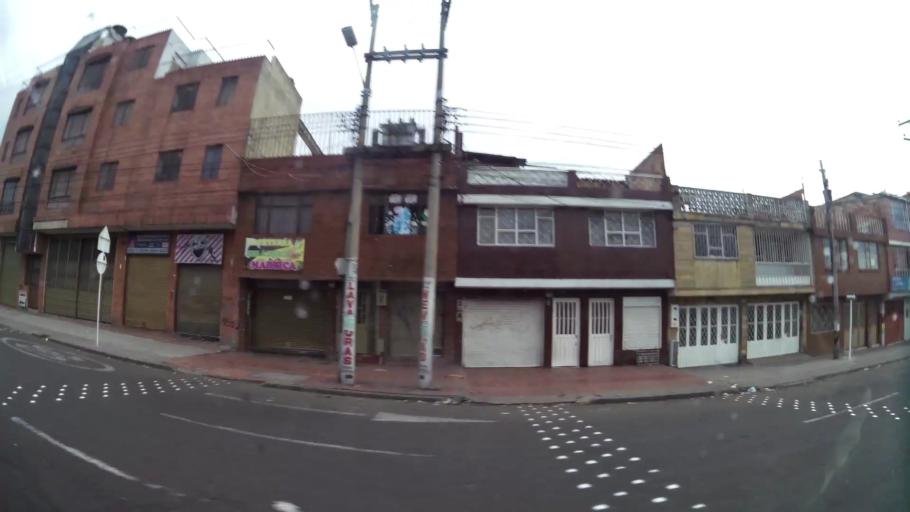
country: CO
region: Bogota D.C.
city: Bogota
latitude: 4.5906
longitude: -74.1436
